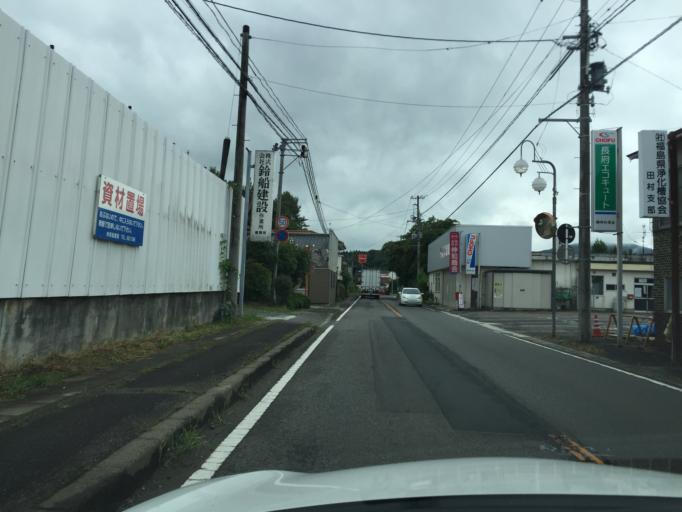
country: JP
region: Fukushima
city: Funehikimachi-funehiki
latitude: 37.4589
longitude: 140.5756
